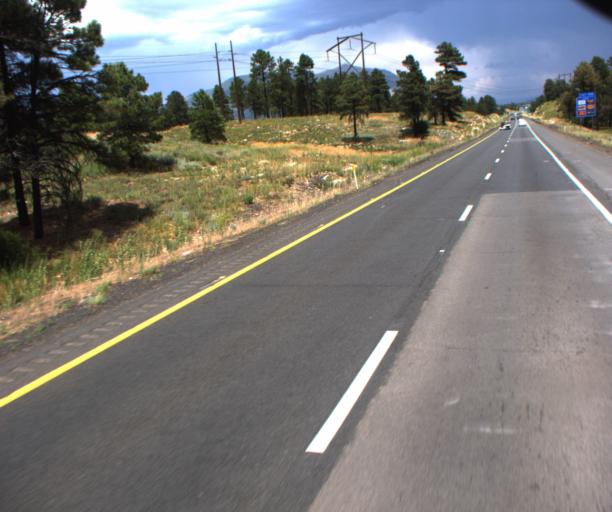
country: US
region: Arizona
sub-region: Coconino County
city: Flagstaff
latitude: 35.1771
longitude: -111.6413
